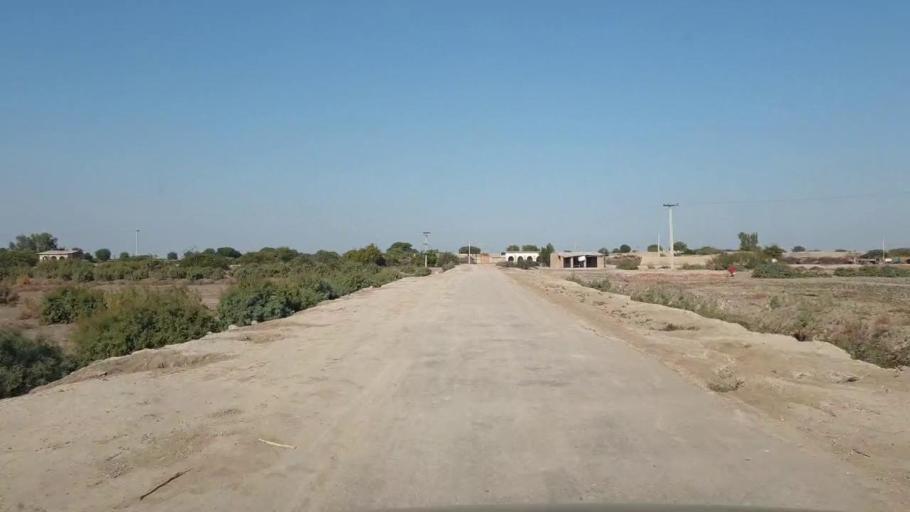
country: PK
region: Sindh
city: Shahpur Chakar
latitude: 26.1564
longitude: 68.6763
